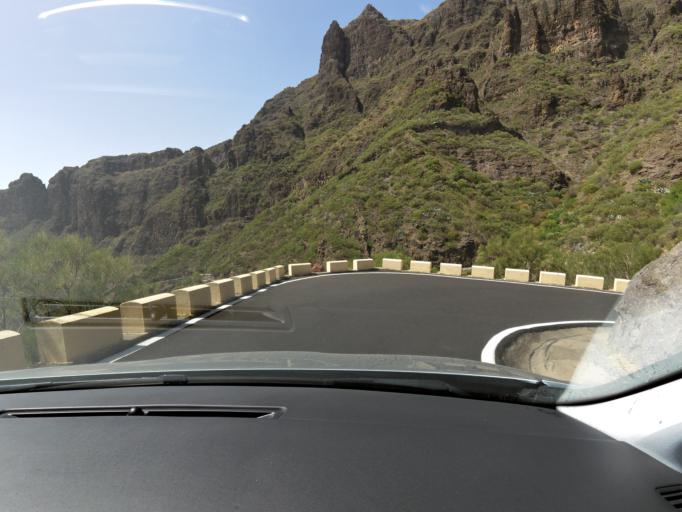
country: ES
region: Canary Islands
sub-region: Provincia de Santa Cruz de Tenerife
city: Santiago del Teide
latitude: 28.3009
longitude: -16.8272
